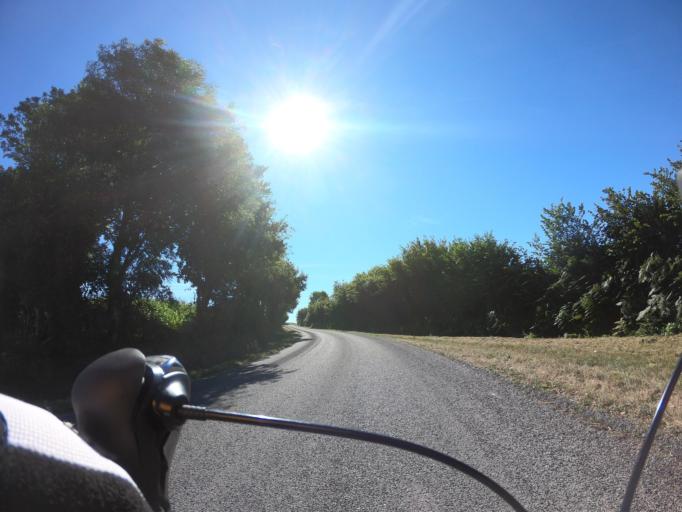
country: FR
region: Pays de la Loire
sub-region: Departement de la Mayenne
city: Pre-en-Pail
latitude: 48.5586
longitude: -0.1285
